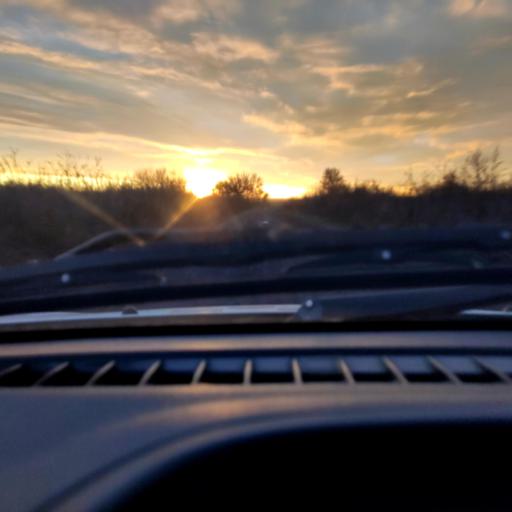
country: RU
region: Samara
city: Tol'yatti
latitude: 53.5950
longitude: 49.4843
